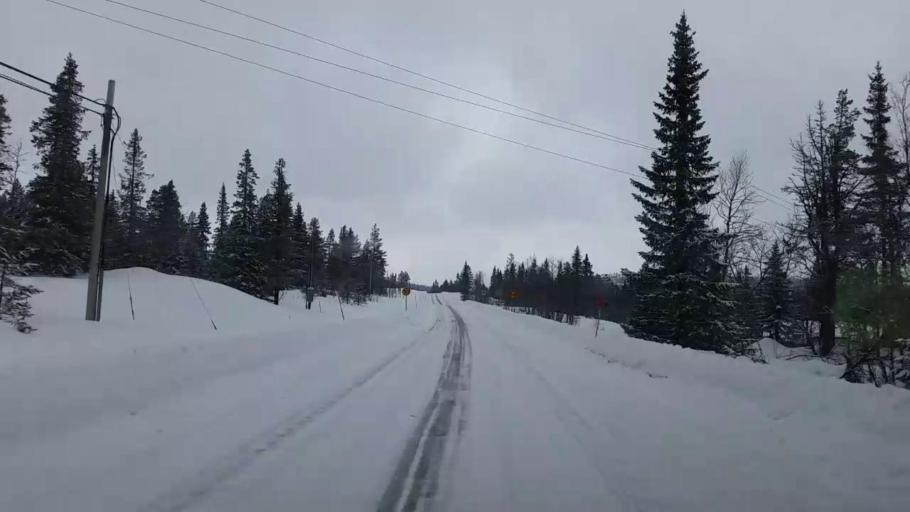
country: SE
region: Jaemtland
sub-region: Bergs Kommun
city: Hoverberg
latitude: 62.4916
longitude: 14.1168
